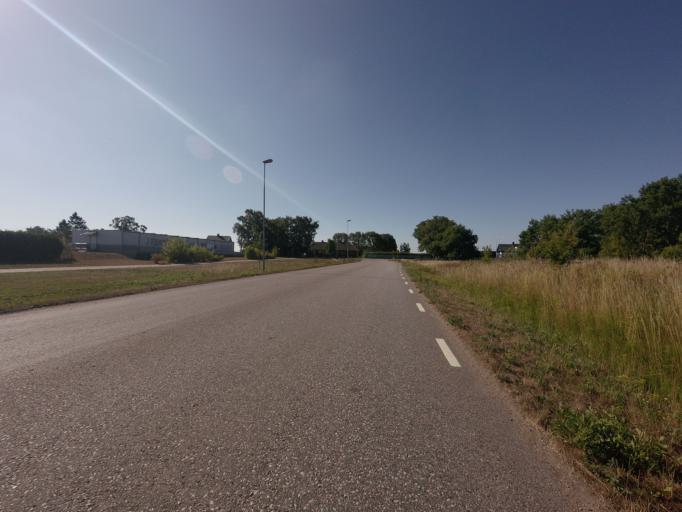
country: SE
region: Skane
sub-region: Trelleborgs Kommun
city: Skare
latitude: 55.4068
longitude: 13.0710
